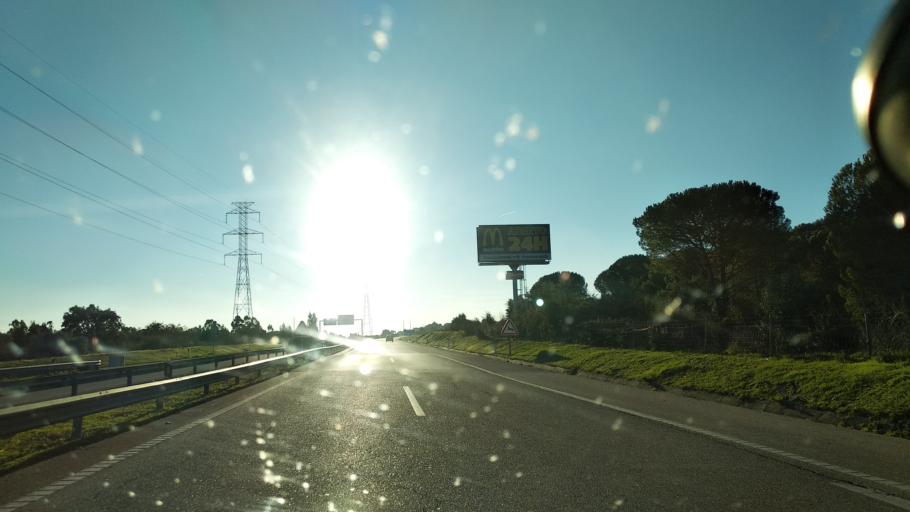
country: PT
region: Santarem
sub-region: Entroncamento
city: Entroncamento
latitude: 39.4739
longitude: -8.4901
